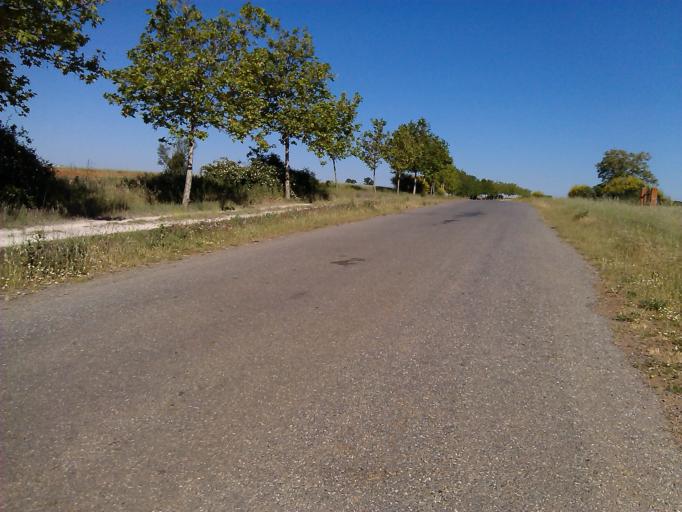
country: ES
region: Castille and Leon
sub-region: Provincia de Leon
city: Bercianos del Real Camino
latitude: 42.3906
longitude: -5.1493
